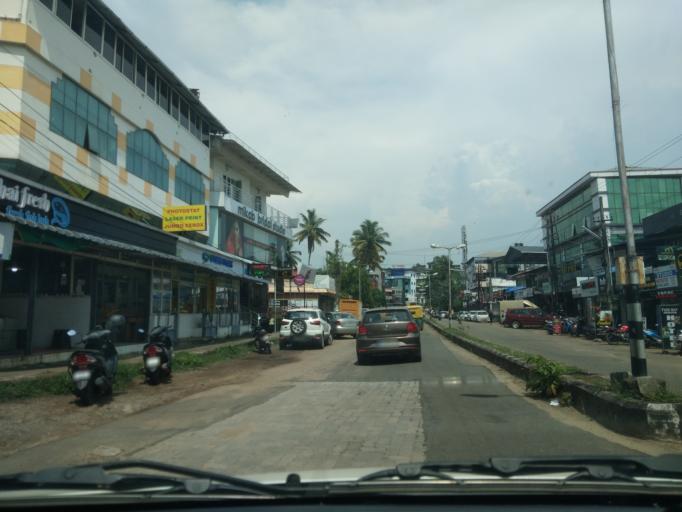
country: IN
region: Kerala
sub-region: Ernakulam
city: Elur
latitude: 10.0466
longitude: 76.3211
